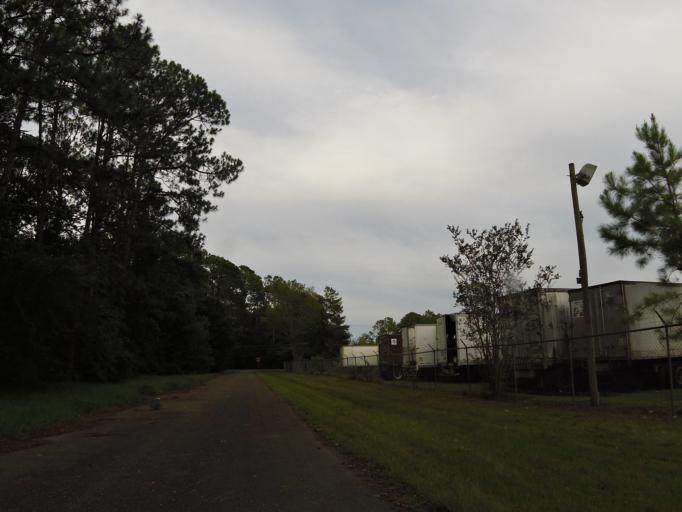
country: US
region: Florida
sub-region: Duval County
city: Jacksonville
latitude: 30.3953
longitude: -81.7537
